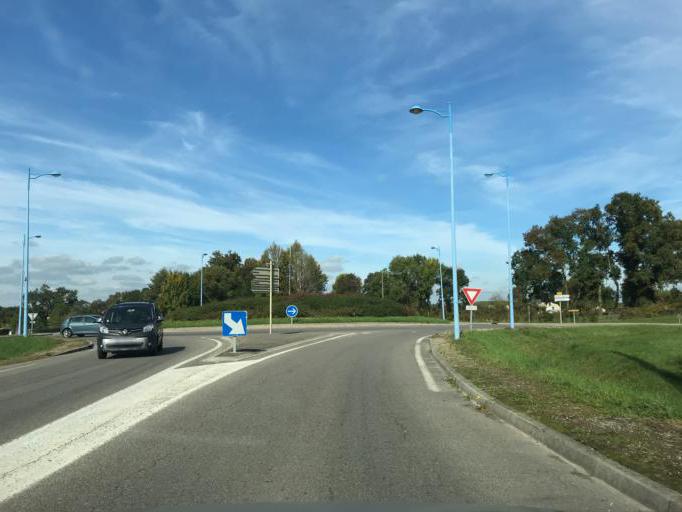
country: FR
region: Rhone-Alpes
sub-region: Departement de l'Ain
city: Montrevel-en-Bresse
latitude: 46.3477
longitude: 5.1258
